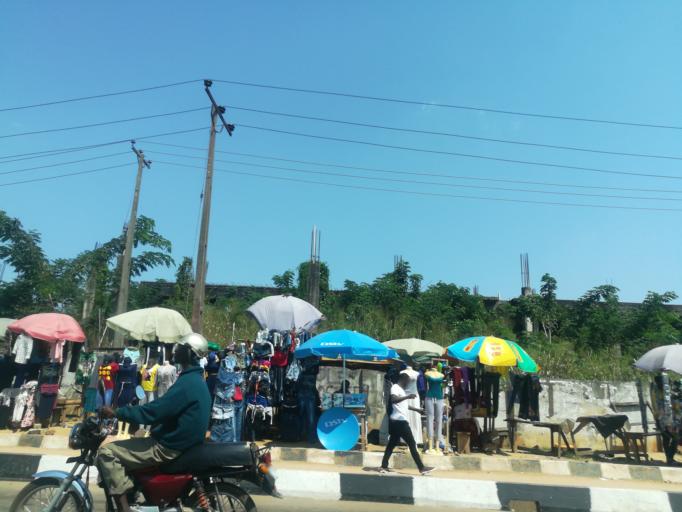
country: NG
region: Ogun
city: Abeokuta
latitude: 7.1335
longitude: 3.3319
